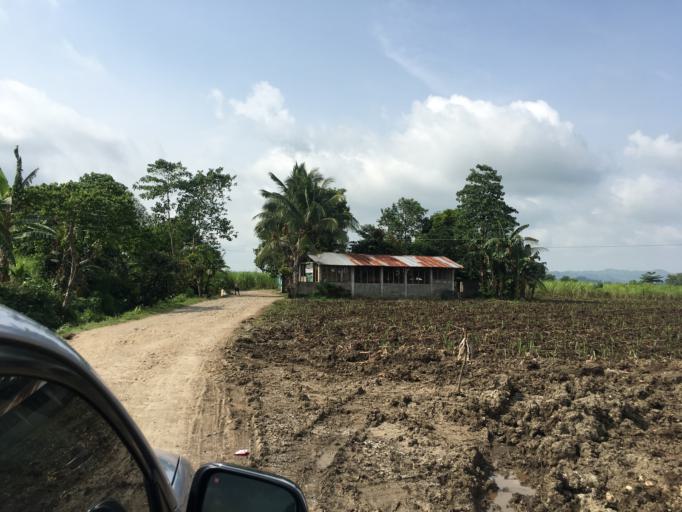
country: PH
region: Western Visayas
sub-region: Province of Negros Occidental
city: Orong
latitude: 9.9531
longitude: 122.8386
